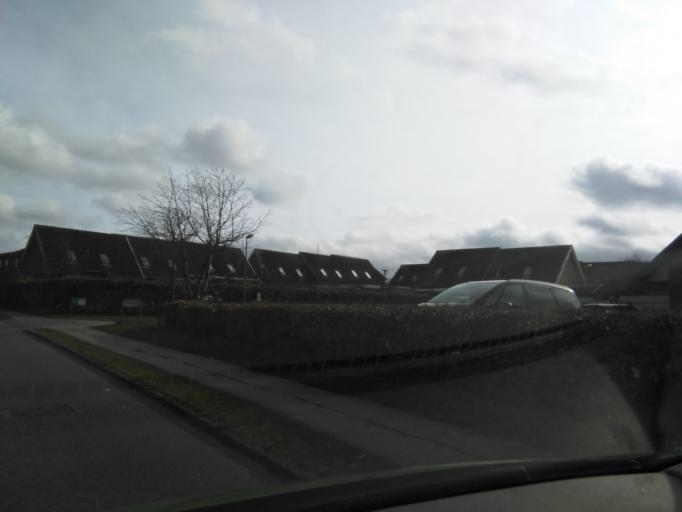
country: DK
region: Central Jutland
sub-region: Arhus Kommune
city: Arhus
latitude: 56.1914
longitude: 10.1938
